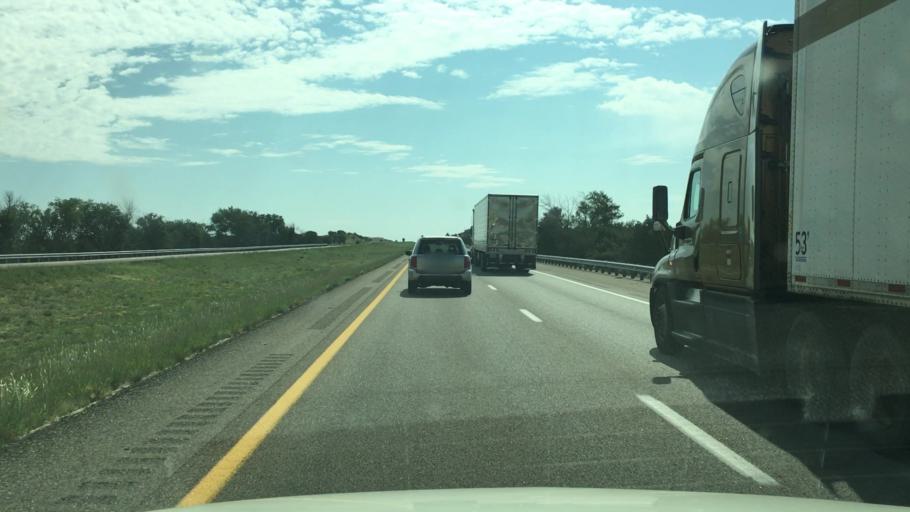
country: US
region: New Mexico
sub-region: Guadalupe County
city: Santa Rosa
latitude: 34.9748
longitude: -104.9609
